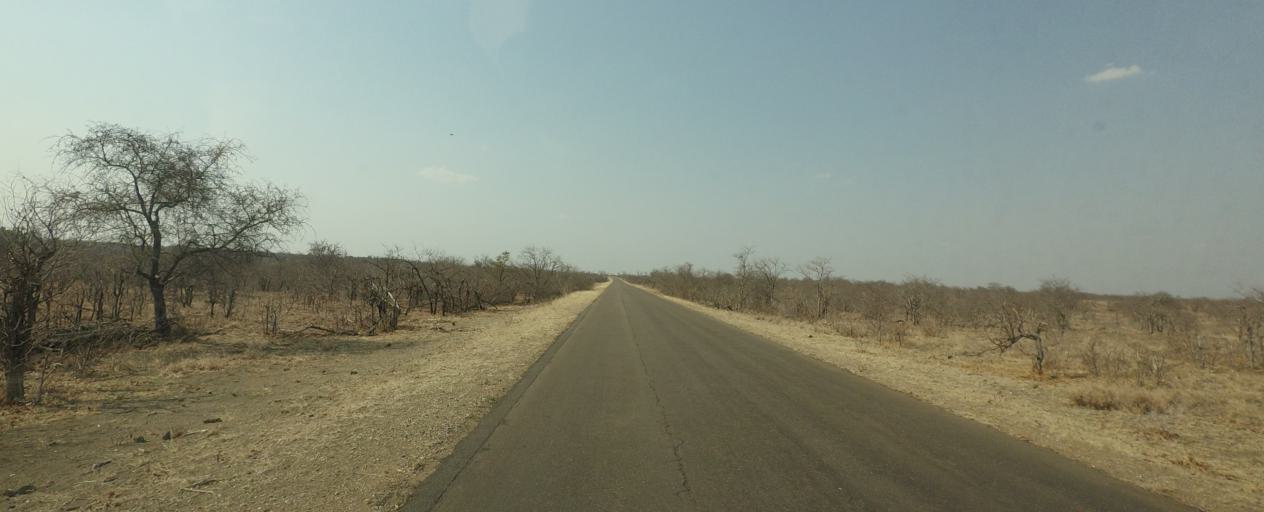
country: ZA
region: Limpopo
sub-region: Mopani District Municipality
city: Giyani
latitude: -23.1269
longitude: 31.3812
